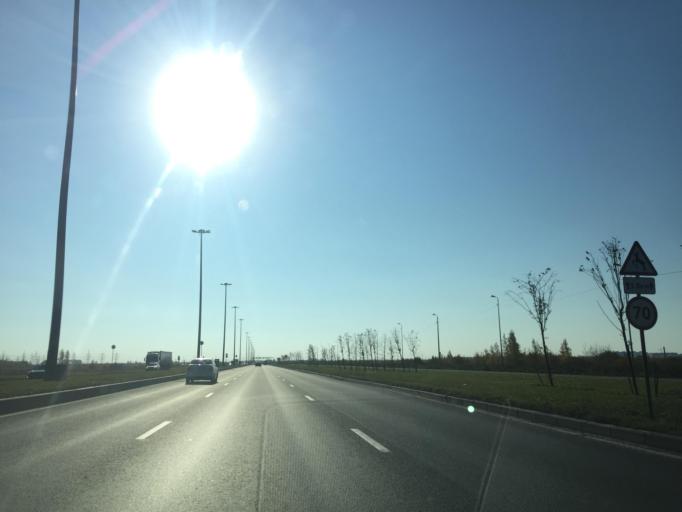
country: RU
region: St.-Petersburg
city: Petro-Slavyanka
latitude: 59.7779
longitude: 30.4981
